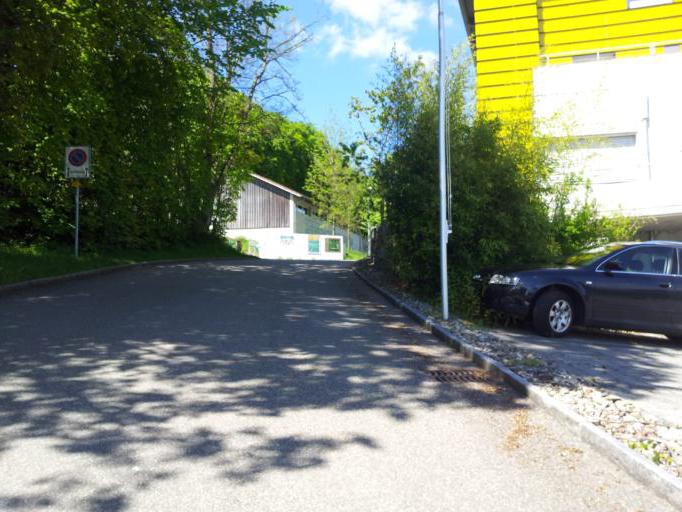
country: CH
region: Aargau
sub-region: Bezirk Bremgarten
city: Rudolfstetten
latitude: 47.3788
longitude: 8.3647
